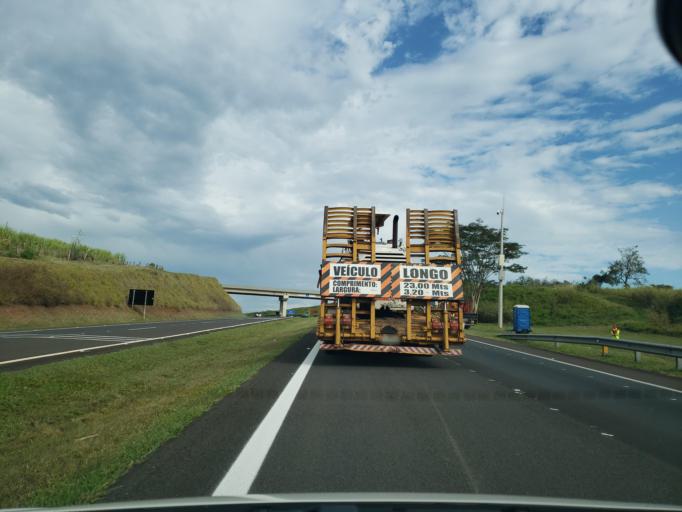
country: BR
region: Sao Paulo
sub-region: Dois Corregos
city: Dois Corregos
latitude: -22.2493
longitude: -48.3572
